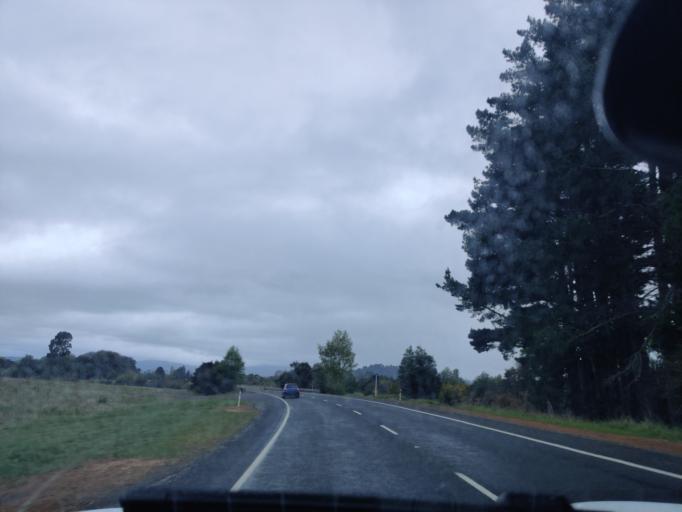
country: NZ
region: Waikato
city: Turangi
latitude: -38.9771
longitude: 175.7733
